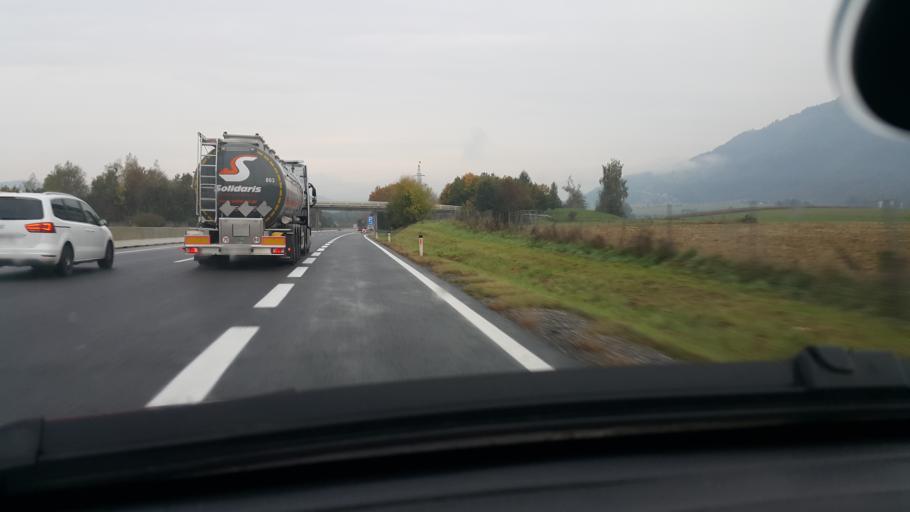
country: AT
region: Carinthia
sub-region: Politischer Bezirk Volkermarkt
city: Voelkermarkt
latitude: 46.6831
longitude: 14.6736
